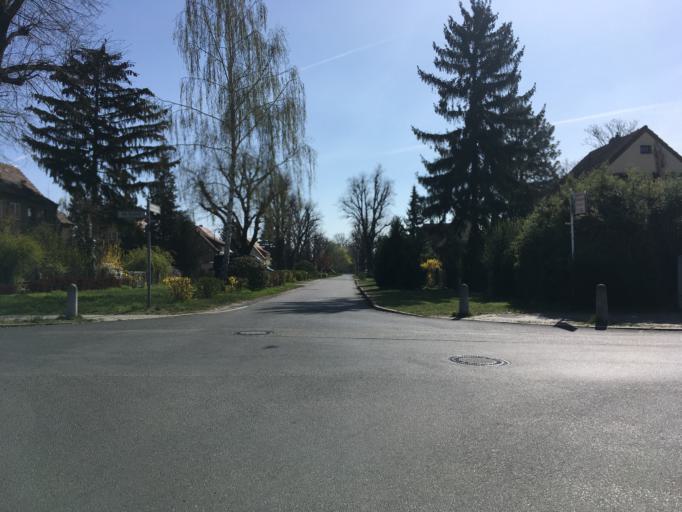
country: DE
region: Berlin
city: Mahlsdorf
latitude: 52.5069
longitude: 13.5996
